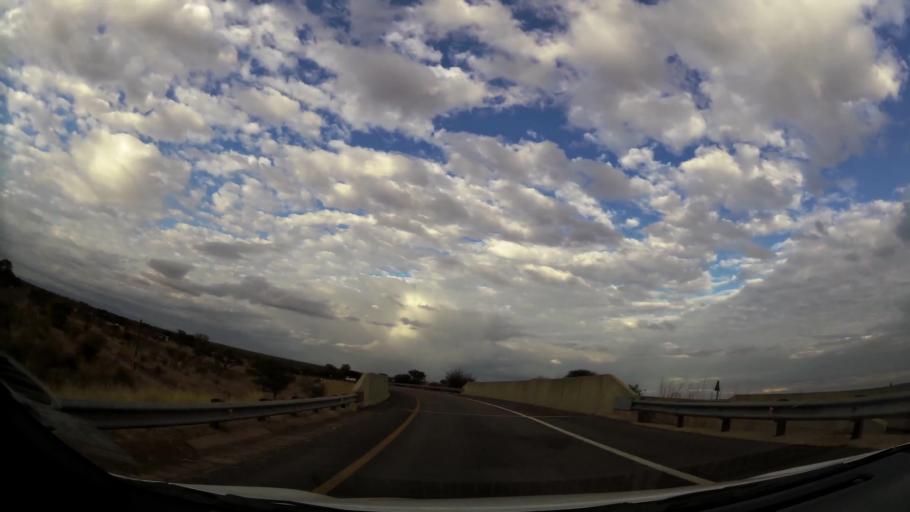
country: ZA
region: Limpopo
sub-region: Waterberg District Municipality
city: Modimolle
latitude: -24.5028
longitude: 28.7323
